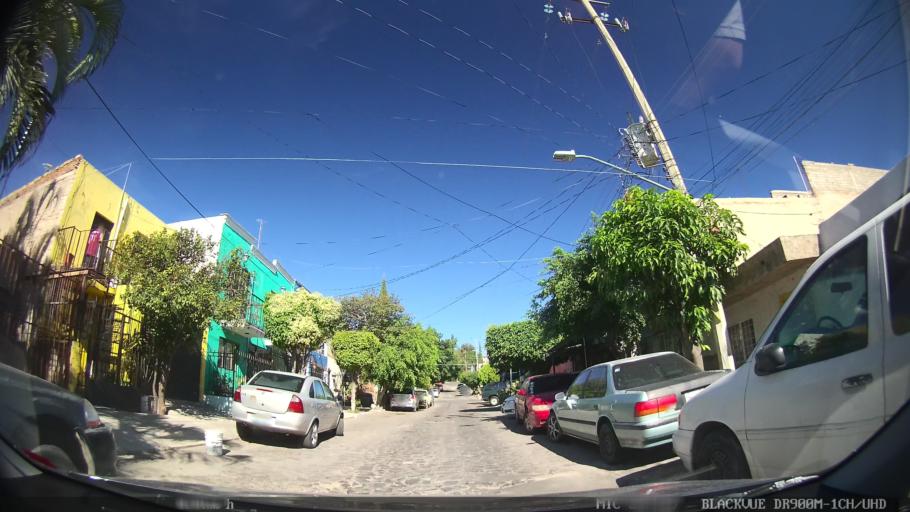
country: MX
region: Jalisco
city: Tlaquepaque
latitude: 20.6893
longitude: -103.2744
